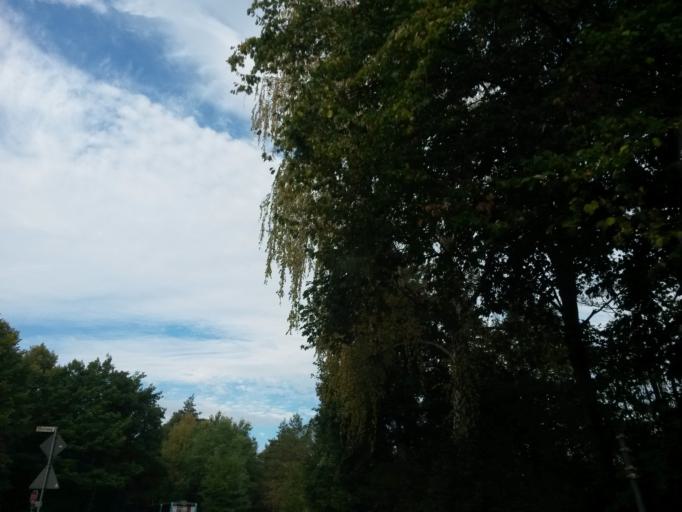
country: DE
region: North Rhine-Westphalia
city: Lohmar
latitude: 50.8369
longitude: 7.1794
